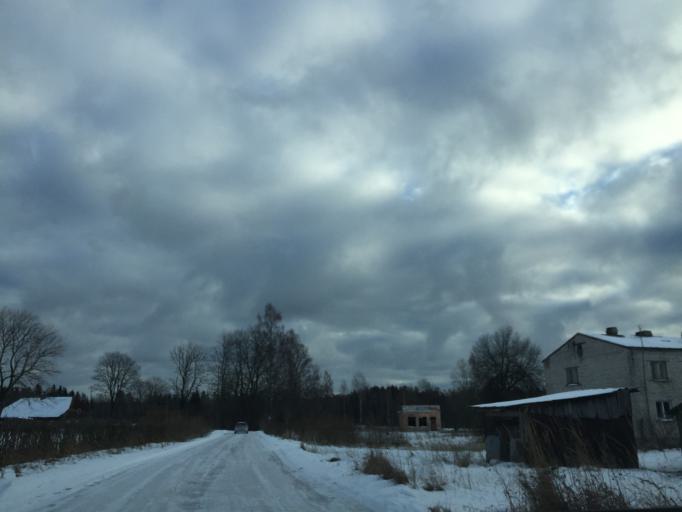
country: LV
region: Lielvarde
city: Lielvarde
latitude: 56.5762
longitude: 24.7949
